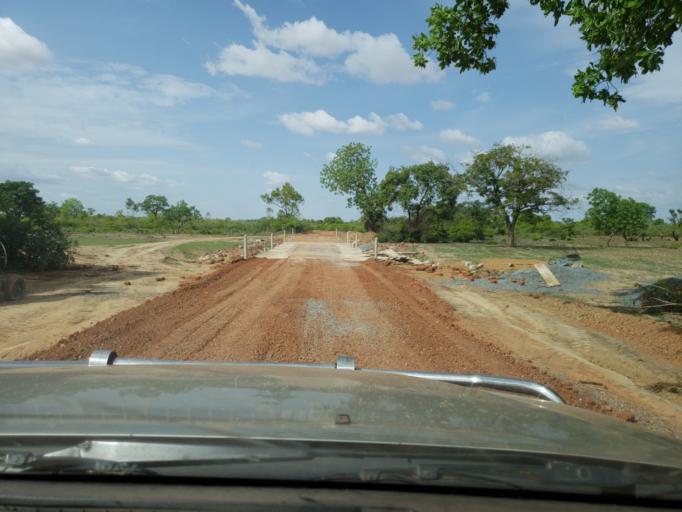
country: ML
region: Segou
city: Bla
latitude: 12.7723
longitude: -5.6151
